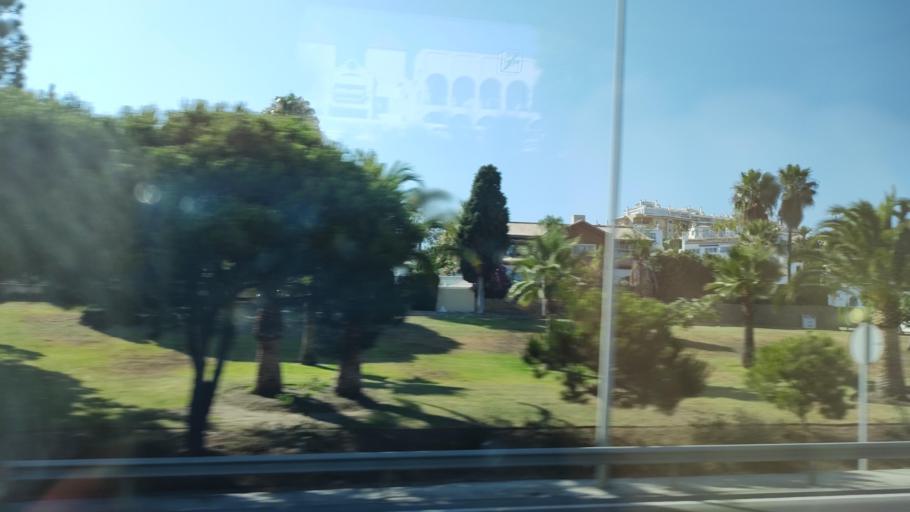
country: ES
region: Andalusia
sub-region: Provincia de Malaga
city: Fuengirola
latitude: 36.4972
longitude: -4.6891
